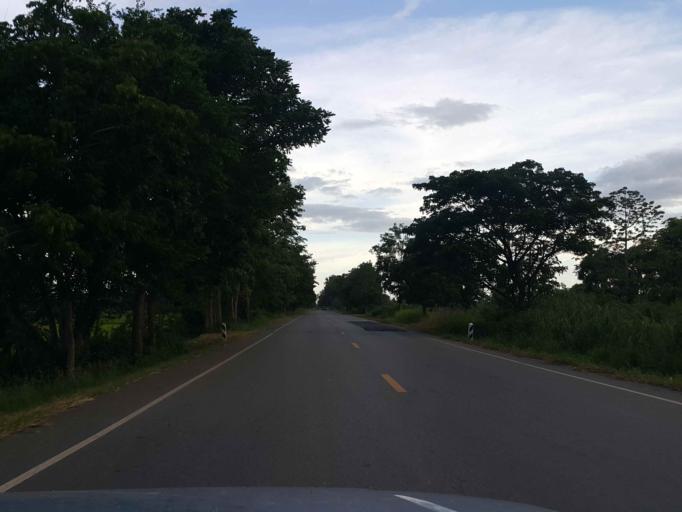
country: TH
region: Sukhothai
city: Sawankhalok
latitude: 17.3637
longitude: 99.7418
